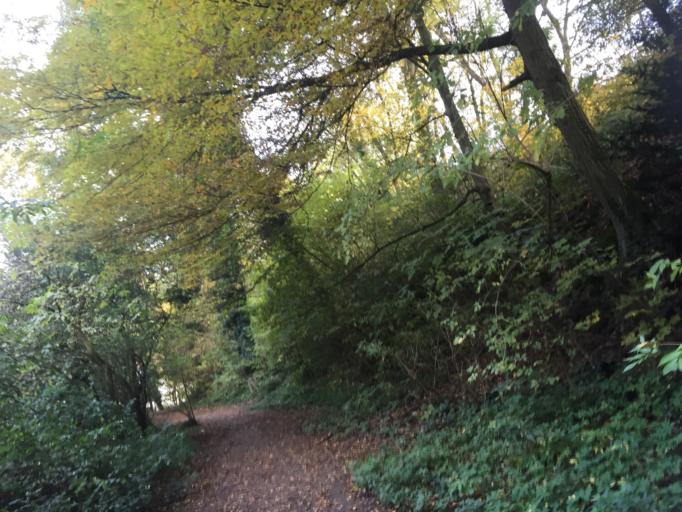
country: DE
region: Hesse
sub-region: Regierungsbezirk Darmstadt
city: Bensheim
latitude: 49.6746
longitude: 8.6322
